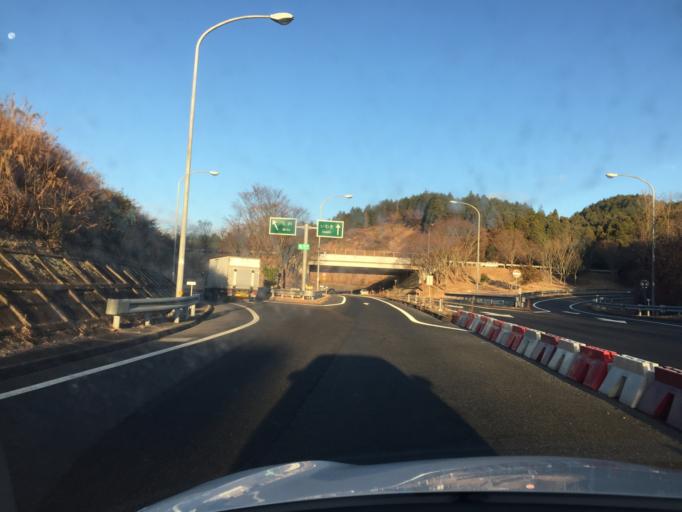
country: JP
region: Ibaraki
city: Kitaibaraki
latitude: 36.7971
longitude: 140.7262
